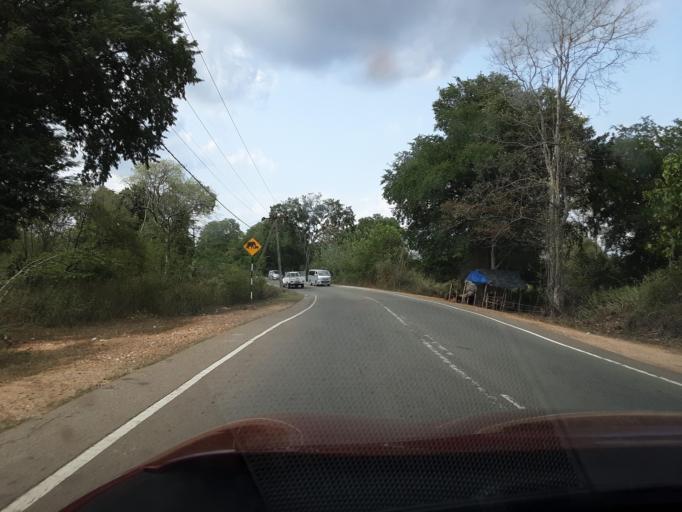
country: LK
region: Uva
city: Haputale
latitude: 6.4966
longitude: 81.1313
